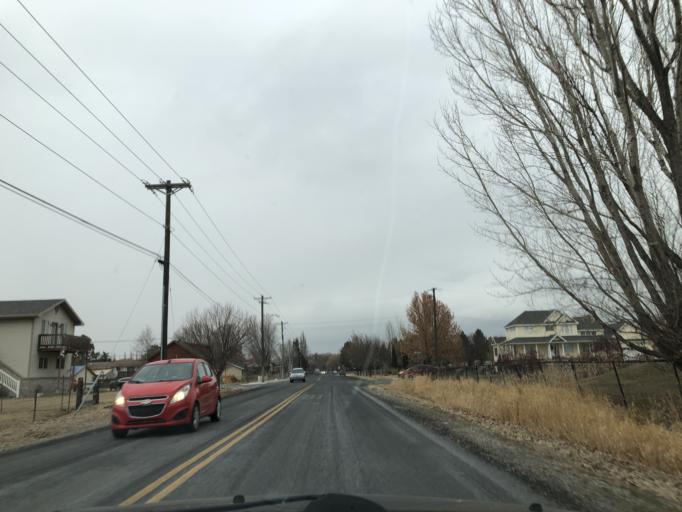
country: US
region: Utah
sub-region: Cache County
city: Logan
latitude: 41.7126
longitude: -111.8529
